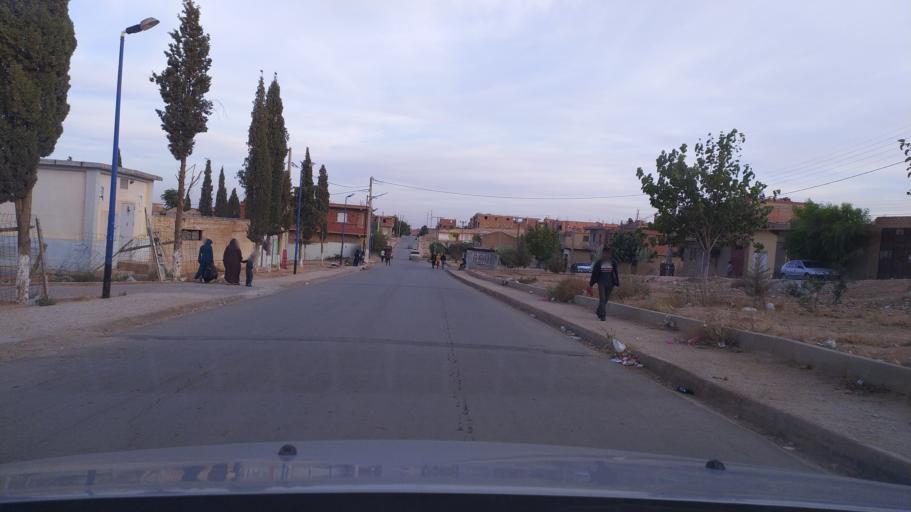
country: DZ
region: Tiaret
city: Frenda
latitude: 34.8940
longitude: 1.2404
